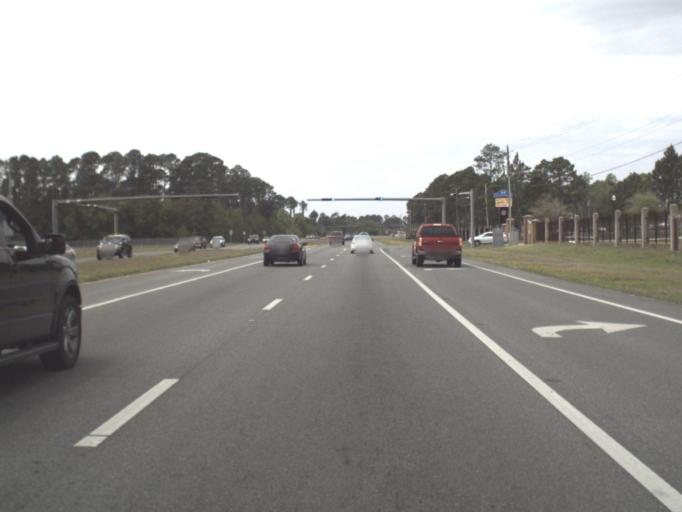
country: US
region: Florida
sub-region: Escambia County
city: Warrington
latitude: 30.3968
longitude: -87.2952
